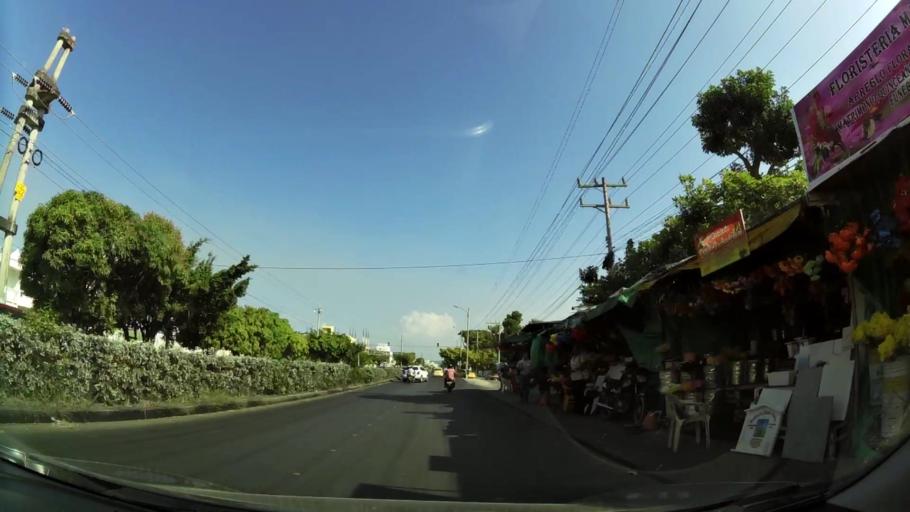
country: CO
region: Bolivar
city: Cartagena
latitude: 10.3882
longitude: -75.4748
